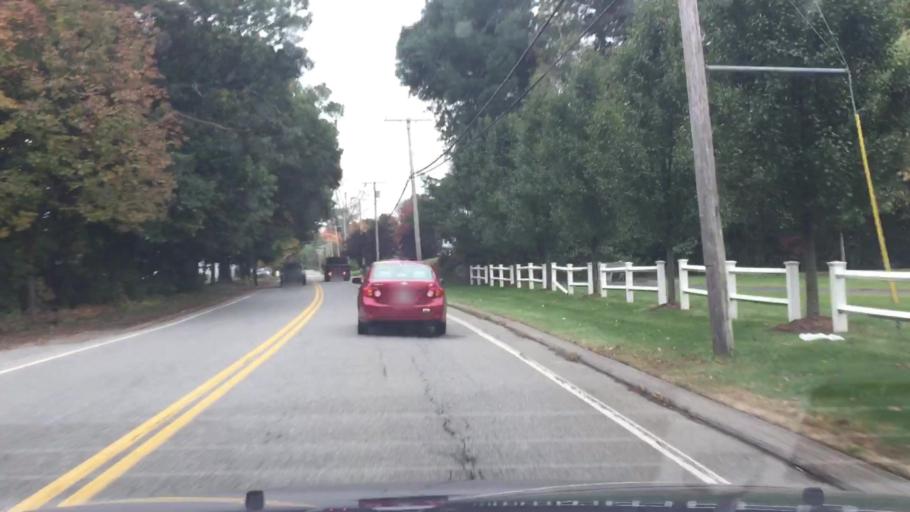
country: US
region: Massachusetts
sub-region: Middlesex County
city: Tyngsboro
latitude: 42.6853
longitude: -71.3726
